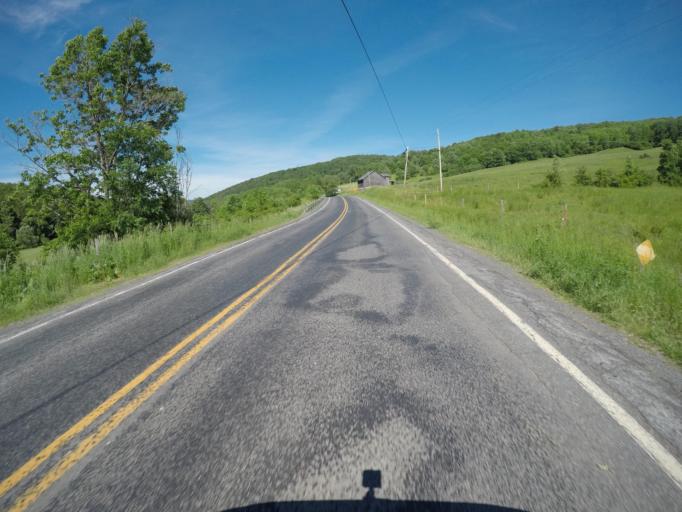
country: US
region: New York
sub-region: Delaware County
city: Delhi
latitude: 42.2120
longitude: -74.9337
